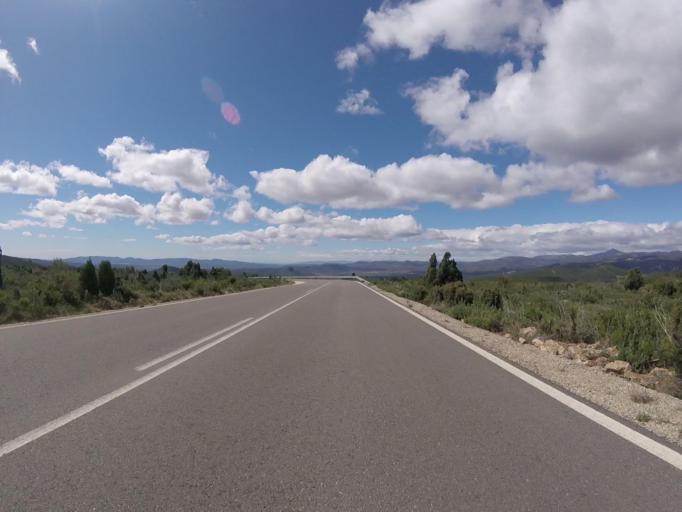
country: ES
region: Valencia
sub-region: Provincia de Castello
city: Culla
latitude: 40.3016
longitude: -0.1268
